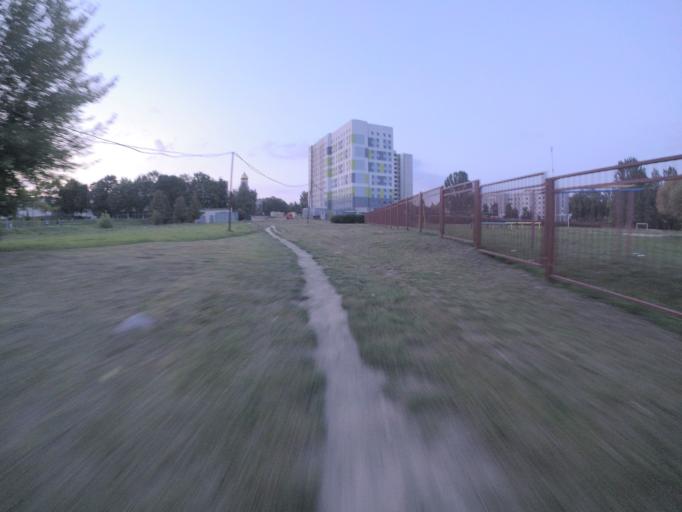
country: BY
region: Grodnenskaya
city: Hrodna
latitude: 53.7019
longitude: 23.8108
